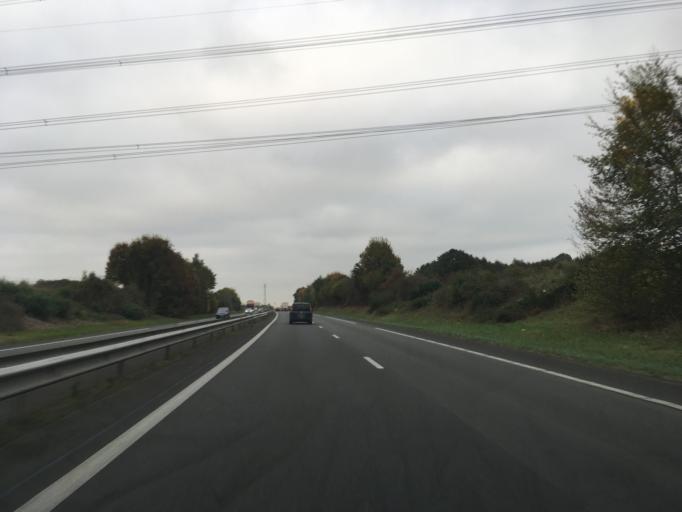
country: FR
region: Pays de la Loire
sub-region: Departement de la Sarthe
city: Noyen-sur-Sarthe
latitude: 47.8476
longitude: -0.1239
